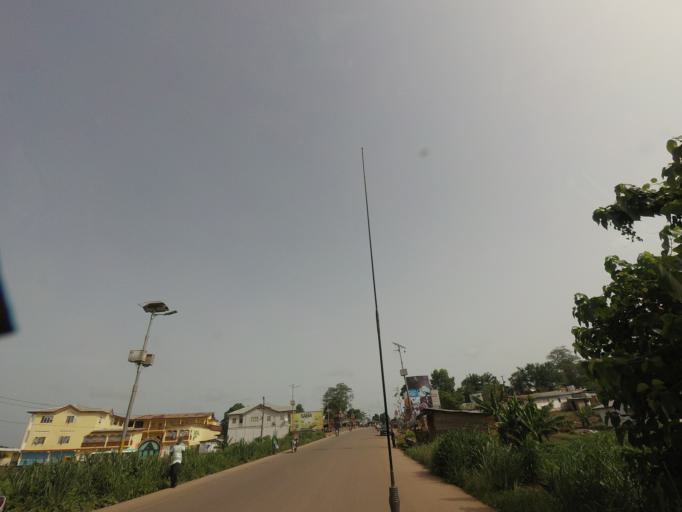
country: SL
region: Southern Province
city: Bo
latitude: 7.9533
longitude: -11.7531
